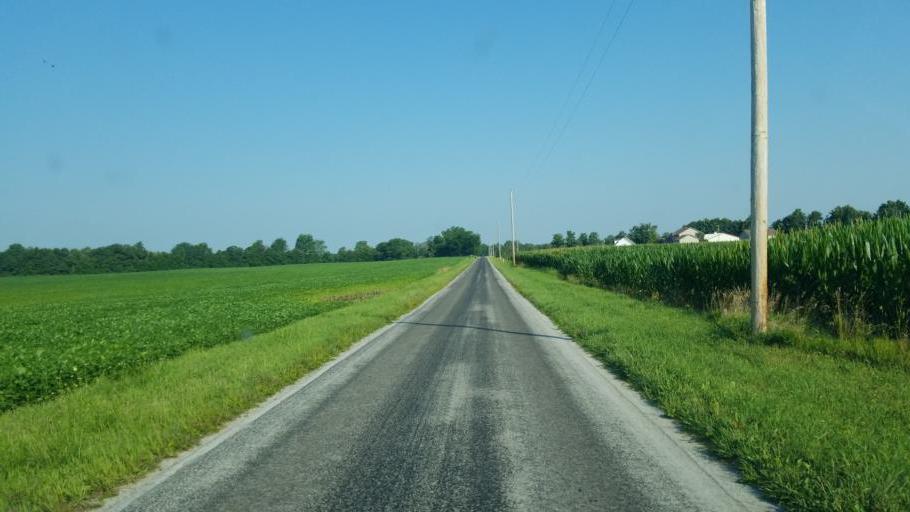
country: US
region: Ohio
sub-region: Hardin County
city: Kenton
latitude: 40.5911
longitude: -83.5325
